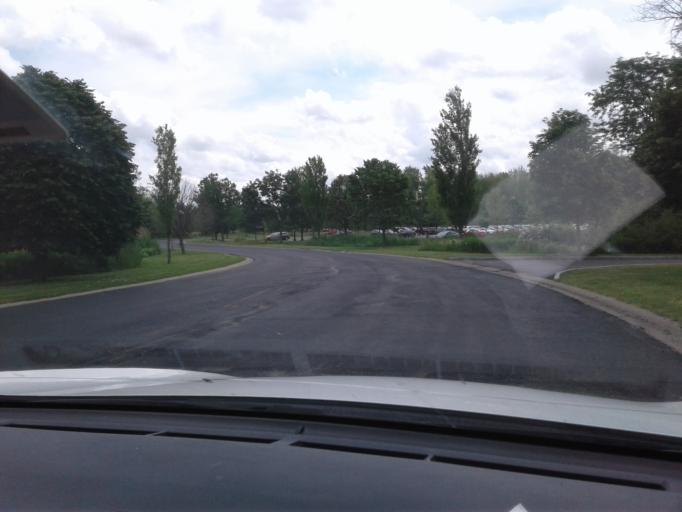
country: US
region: New York
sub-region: Onondaga County
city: East Syracuse
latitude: 43.0892
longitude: -76.0767
